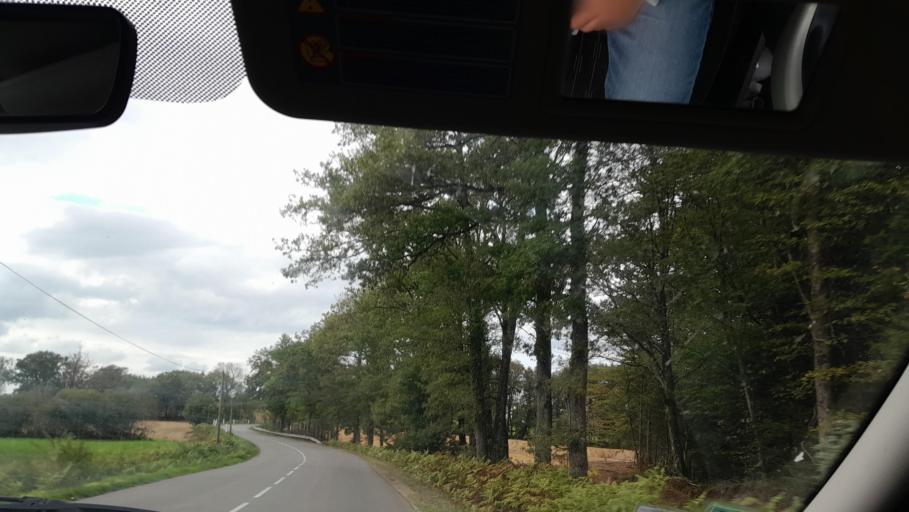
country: FR
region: Brittany
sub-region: Departement d'Ille-et-Vilaine
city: Le Pertre
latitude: 48.0466
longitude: -1.0873
